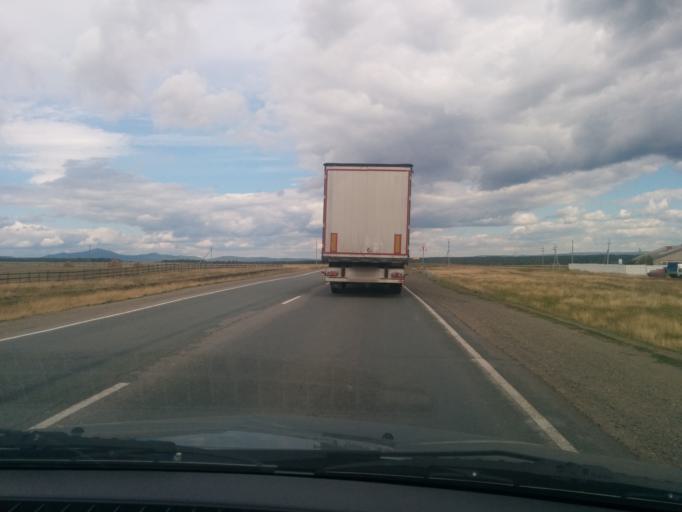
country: RU
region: Bashkortostan
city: Lomovka
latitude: 53.8811
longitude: 58.1128
